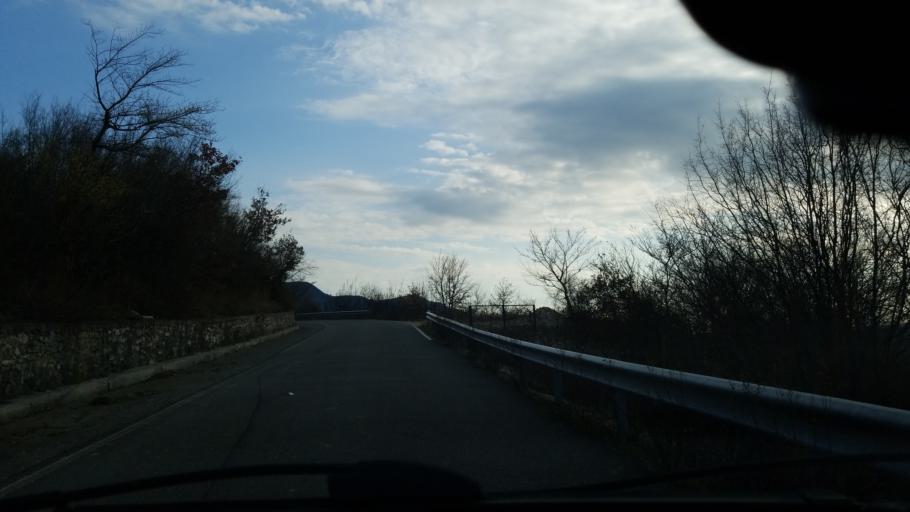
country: AL
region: Lezhe
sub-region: Rrethi i Lezhes
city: Kallmeti i Madh
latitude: 41.8757
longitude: 19.6951
